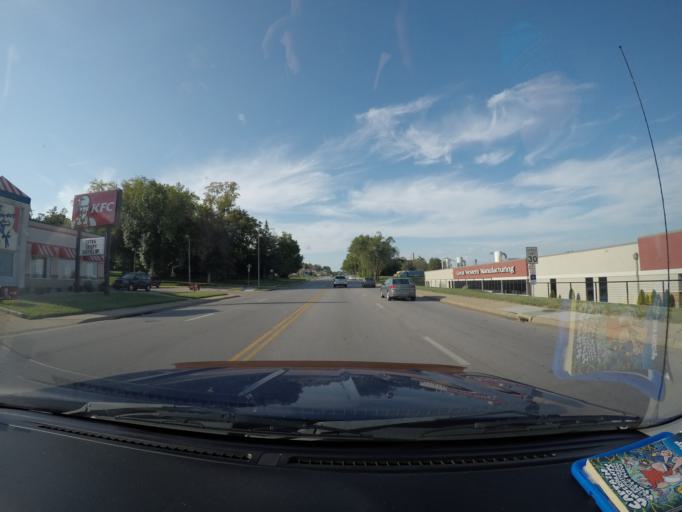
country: US
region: Kansas
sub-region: Leavenworth County
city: Leavenworth
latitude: 39.2964
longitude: -94.9089
